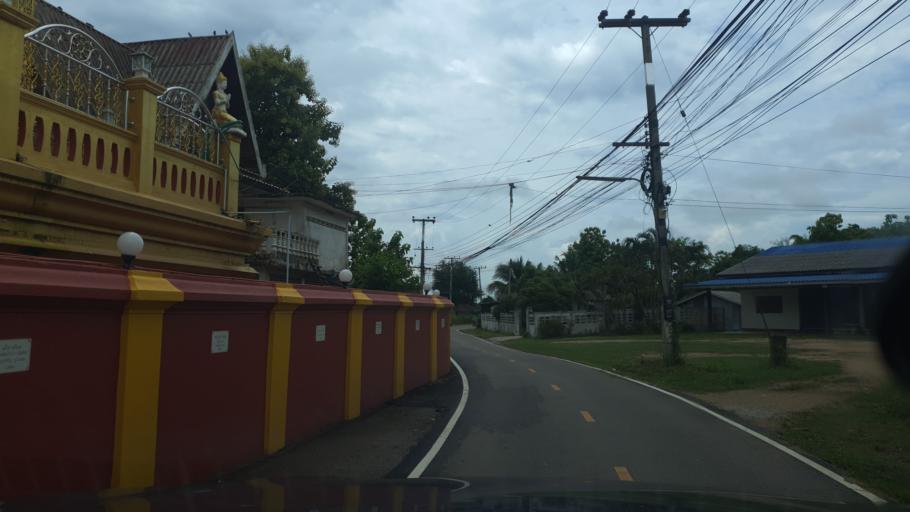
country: TH
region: Lampang
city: Hang Chat
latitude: 18.3099
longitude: 99.3536
